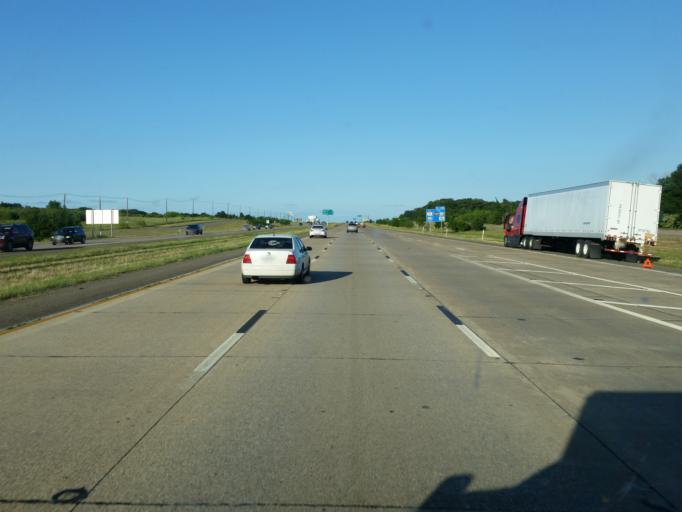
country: US
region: Texas
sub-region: Dallas County
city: Balch Springs
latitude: 32.7029
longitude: -96.6003
